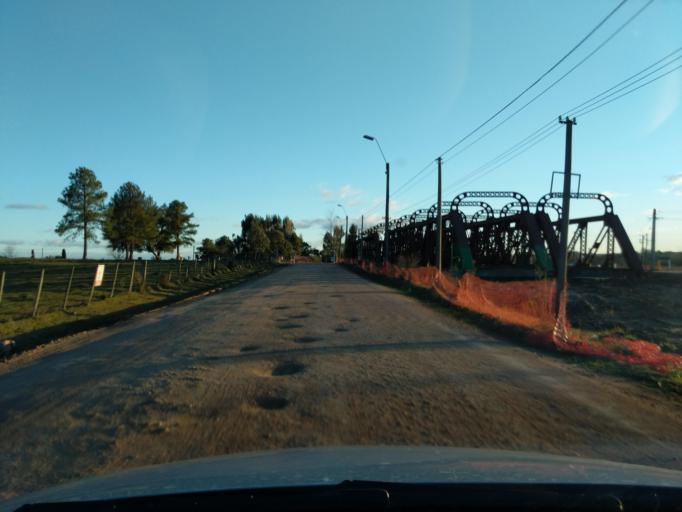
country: UY
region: Florida
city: Florida
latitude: -34.1037
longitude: -56.2415
